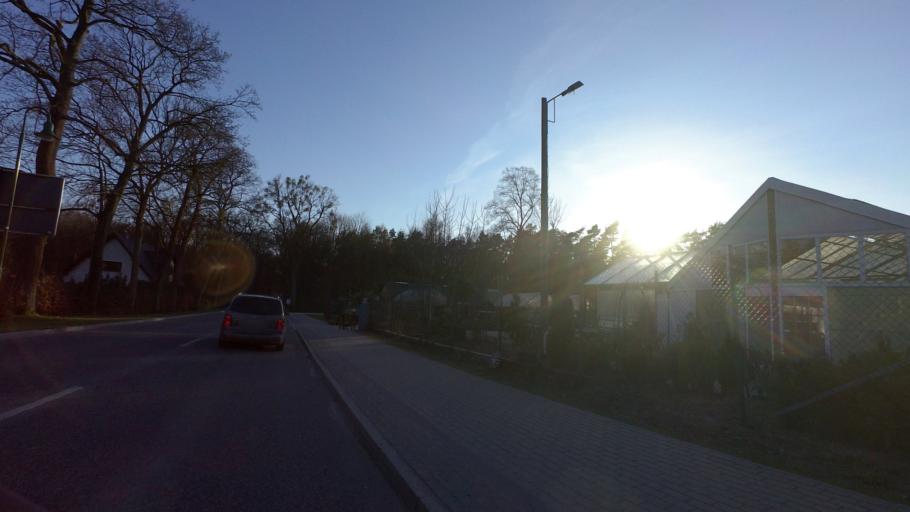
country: DE
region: Brandenburg
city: Werftpfuhl
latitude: 52.6798
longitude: 13.8353
